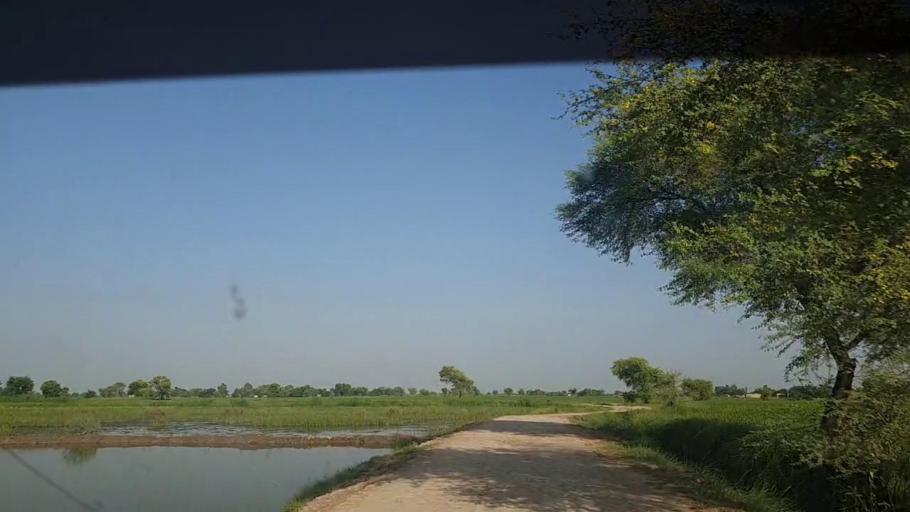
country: PK
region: Sindh
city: Tangwani
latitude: 28.2703
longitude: 69.0088
